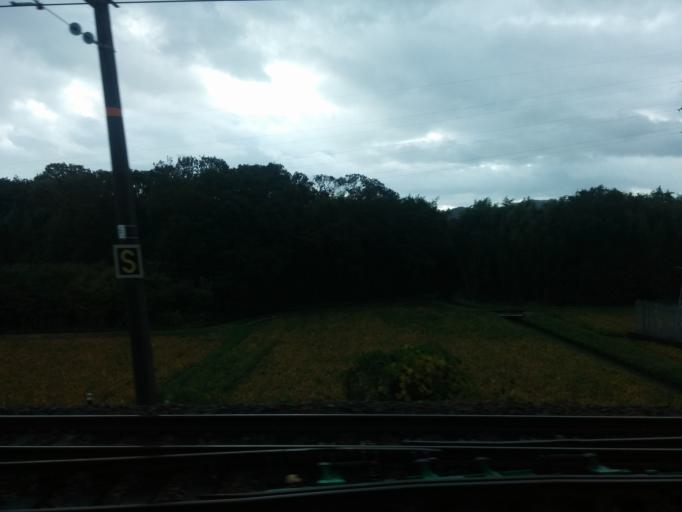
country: JP
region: Shiga Prefecture
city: Omihachiman
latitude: 35.0974
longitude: 136.0684
